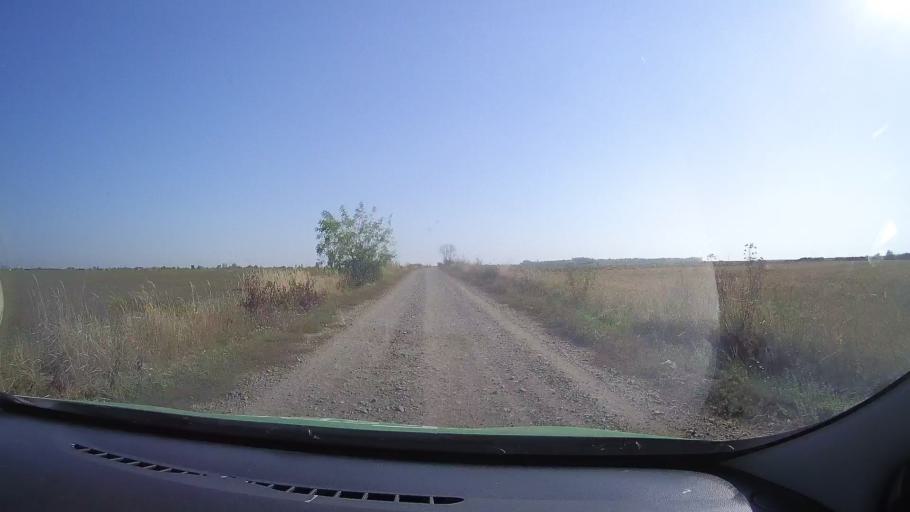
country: RO
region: Satu Mare
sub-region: Comuna Berveni
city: Berveni
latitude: 47.7359
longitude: 22.4450
